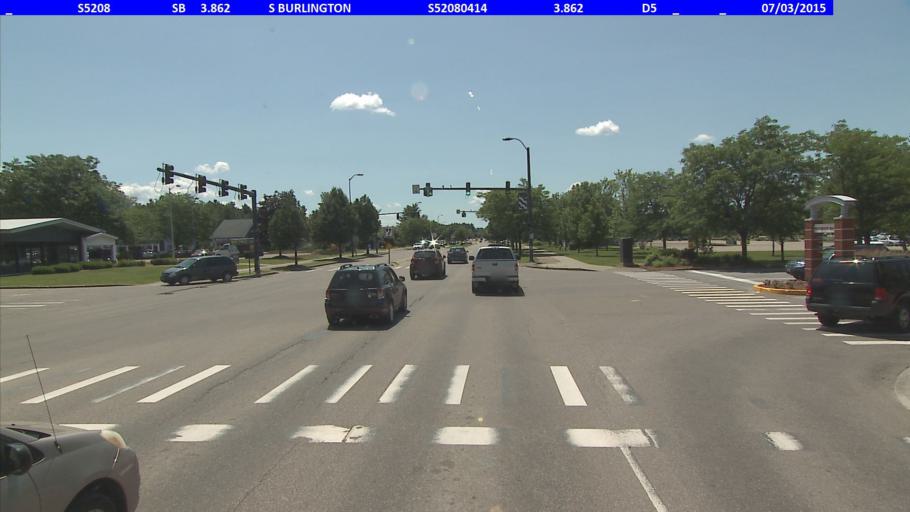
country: US
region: Vermont
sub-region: Chittenden County
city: South Burlington
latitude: 44.4657
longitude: -73.1812
